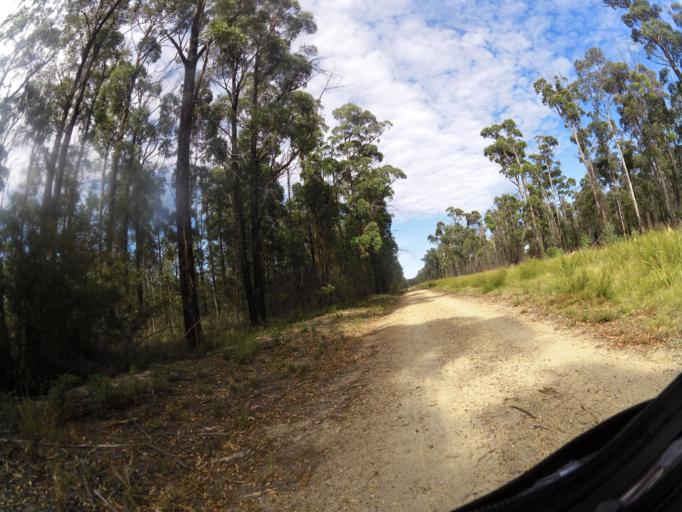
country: AU
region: Victoria
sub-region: East Gippsland
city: Lakes Entrance
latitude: -37.7463
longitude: 148.2360
